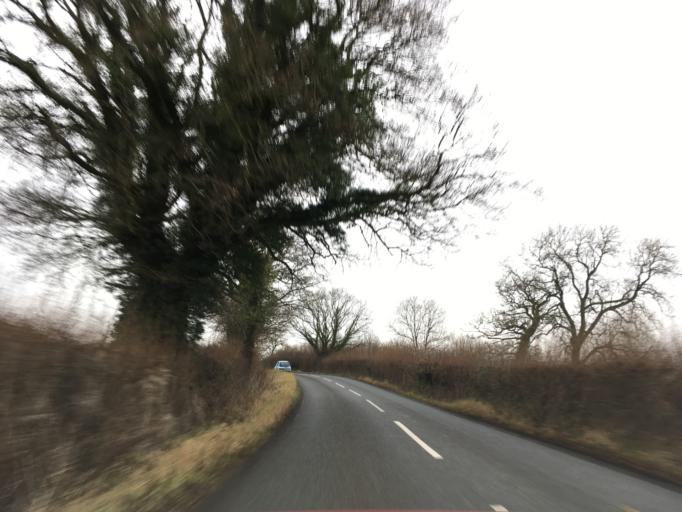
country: GB
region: England
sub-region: Gloucestershire
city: Wotton-under-Edge
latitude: 51.6093
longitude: -2.3434
